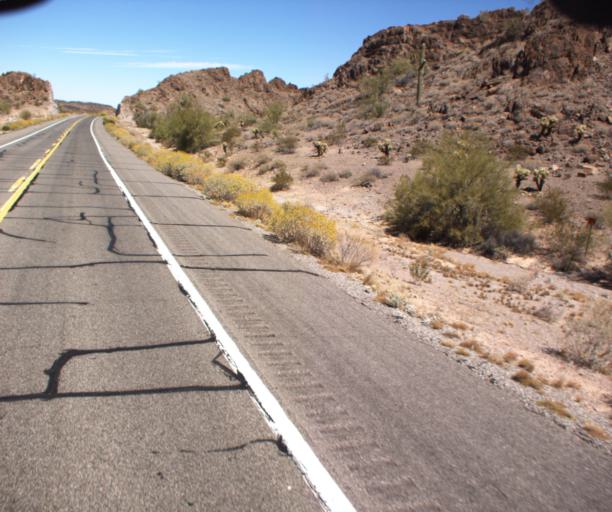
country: US
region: Arizona
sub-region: Pima County
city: Ajo
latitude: 32.5479
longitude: -112.8800
